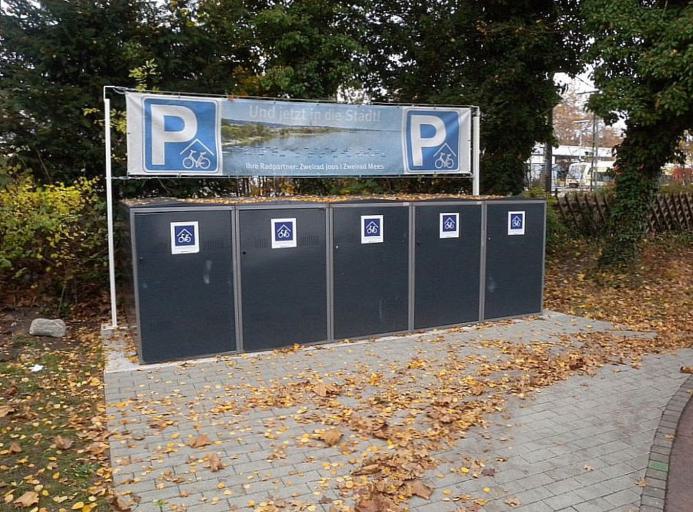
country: DE
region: Baden-Wuerttemberg
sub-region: Freiburg Region
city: Radolfzell am Bodensee
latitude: 47.7358
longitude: 8.9681
